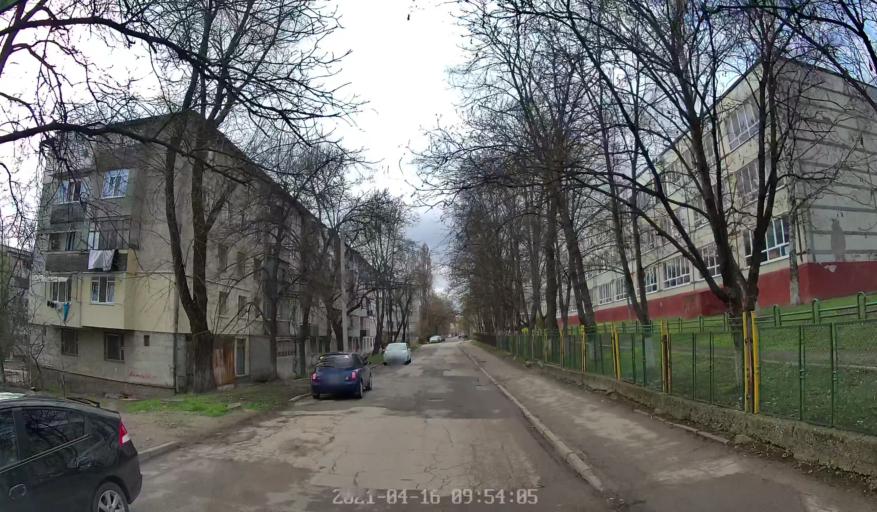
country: MD
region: Chisinau
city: Stauceni
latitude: 47.0583
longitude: 28.8447
